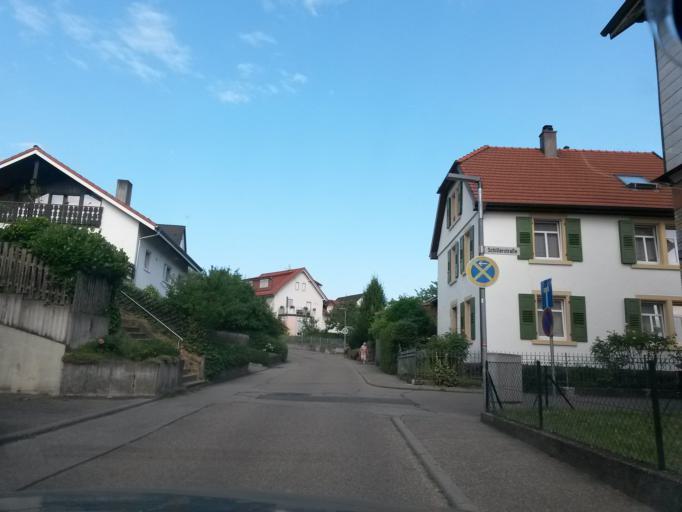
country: DE
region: Baden-Wuerttemberg
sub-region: Karlsruhe Region
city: Birkenfeld
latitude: 48.8962
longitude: 8.5993
